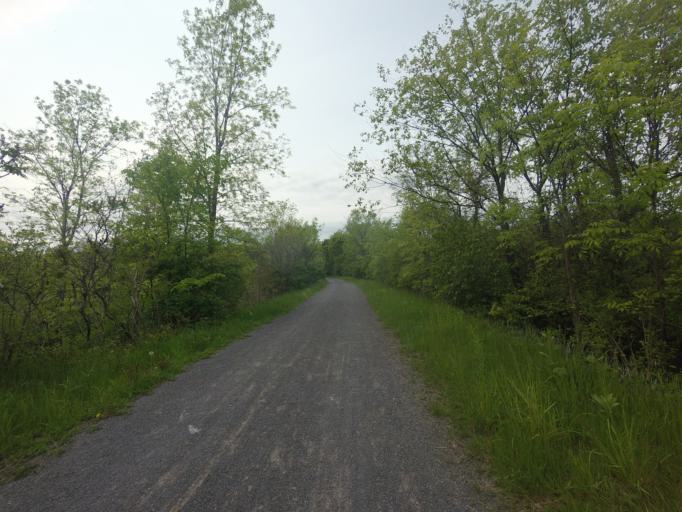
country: CA
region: Ontario
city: Kingston
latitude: 44.3028
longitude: -76.5592
